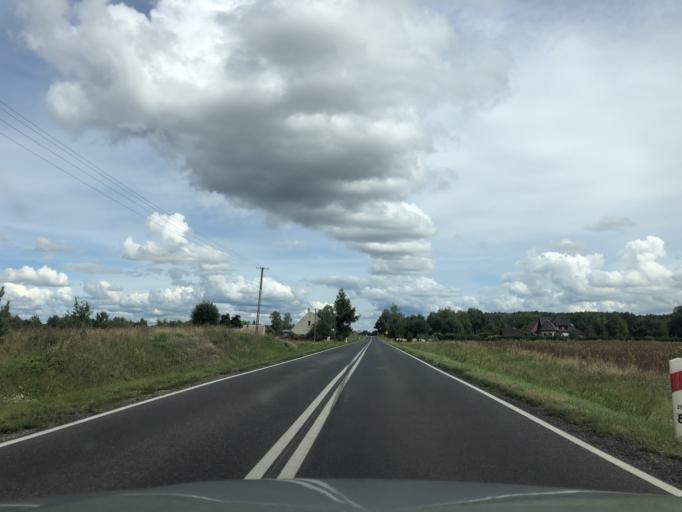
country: PL
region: Greater Poland Voivodeship
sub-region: Powiat czarnkowsko-trzcianecki
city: Trzcianka
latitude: 53.0614
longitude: 16.5203
